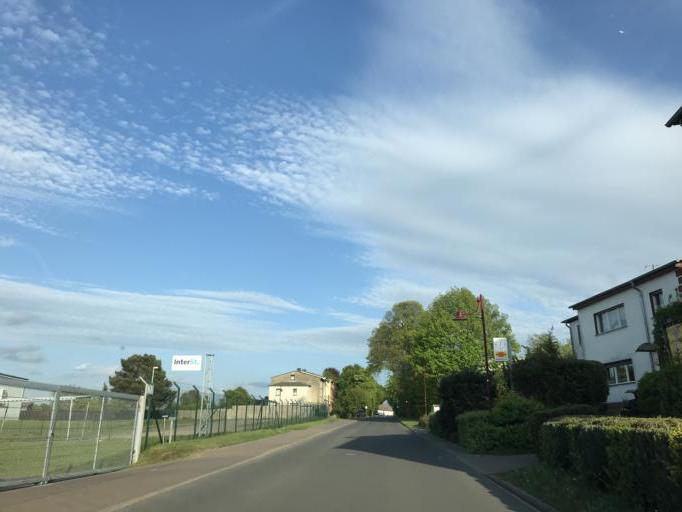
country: DE
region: Brandenburg
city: Joachimsthal
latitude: 52.9723
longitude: 13.7428
